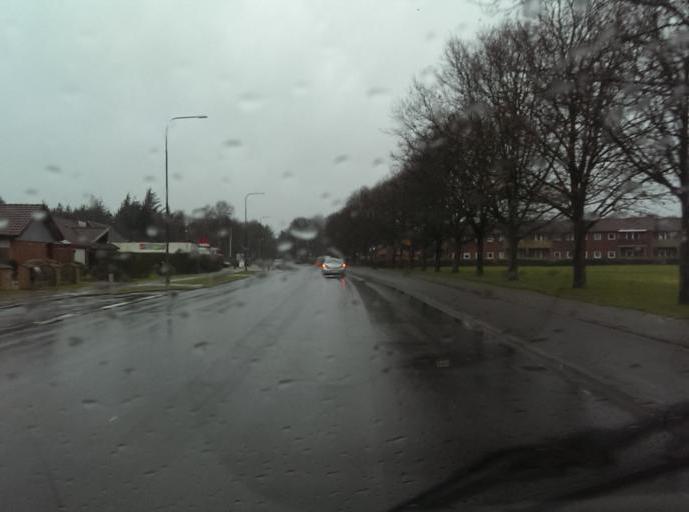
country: DK
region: South Denmark
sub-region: Esbjerg Kommune
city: Esbjerg
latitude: 55.4967
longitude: 8.4463
